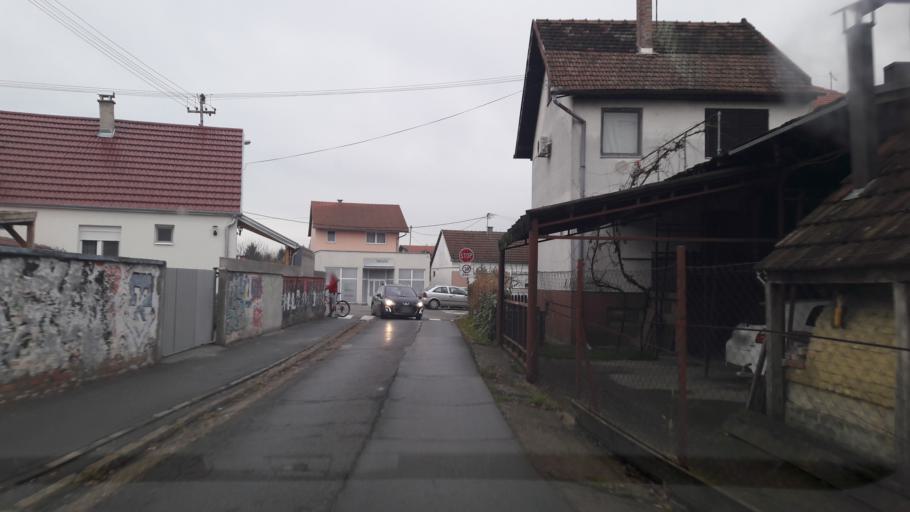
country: HR
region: Osjecko-Baranjska
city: Visnjevac
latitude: 45.5633
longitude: 18.6185
